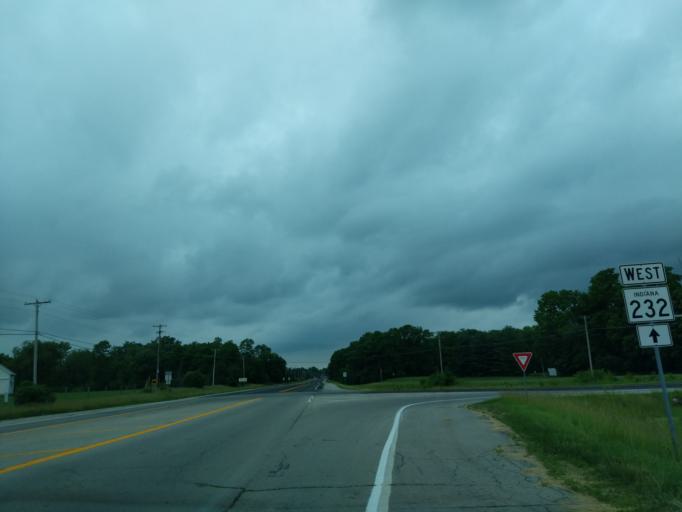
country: US
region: Indiana
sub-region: Madison County
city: Chesterfield
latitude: 40.0913
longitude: -85.6236
